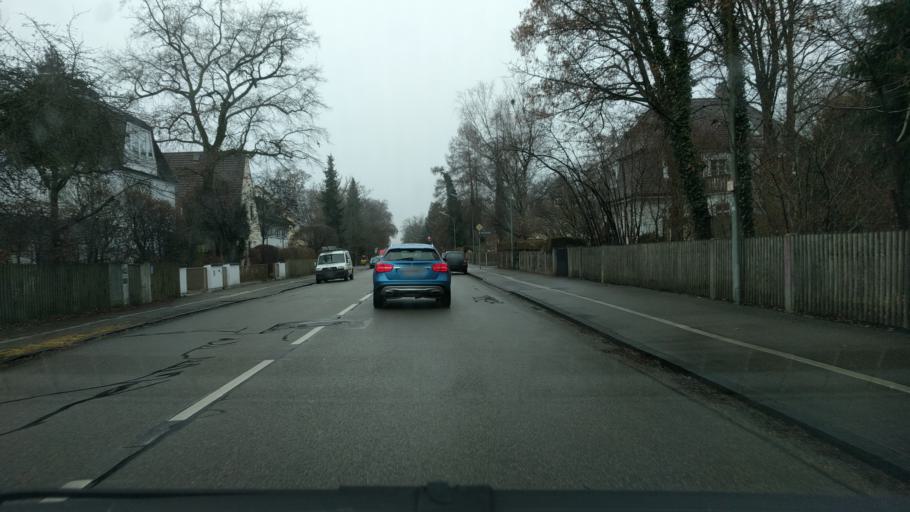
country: DE
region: Bavaria
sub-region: Upper Bavaria
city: Pullach im Isartal
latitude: 48.0828
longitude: 11.5195
